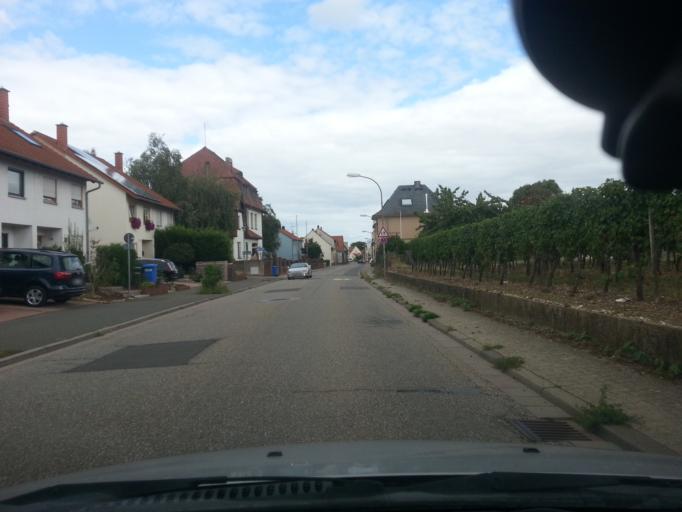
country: DE
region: Rheinland-Pfalz
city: Kleinkarlbach
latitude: 49.5459
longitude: 8.1546
